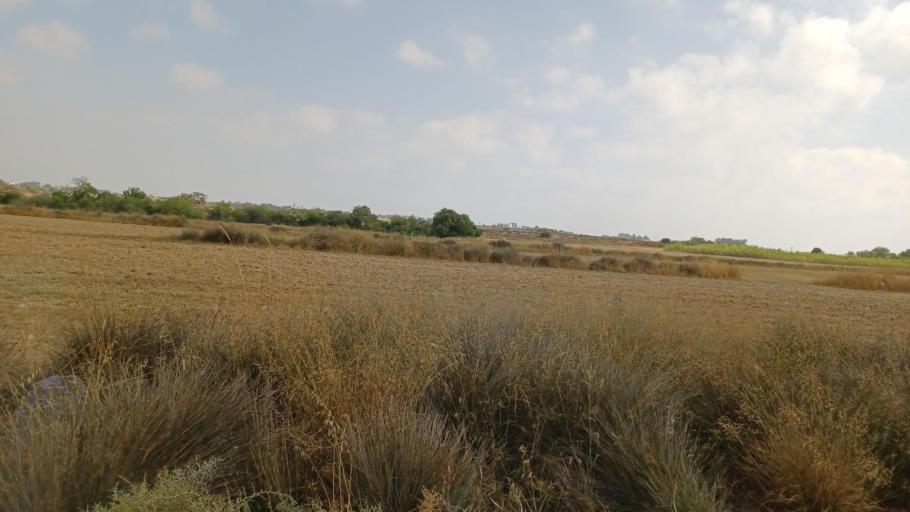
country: CY
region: Ammochostos
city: Paralimni
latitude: 35.0168
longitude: 34.0026
